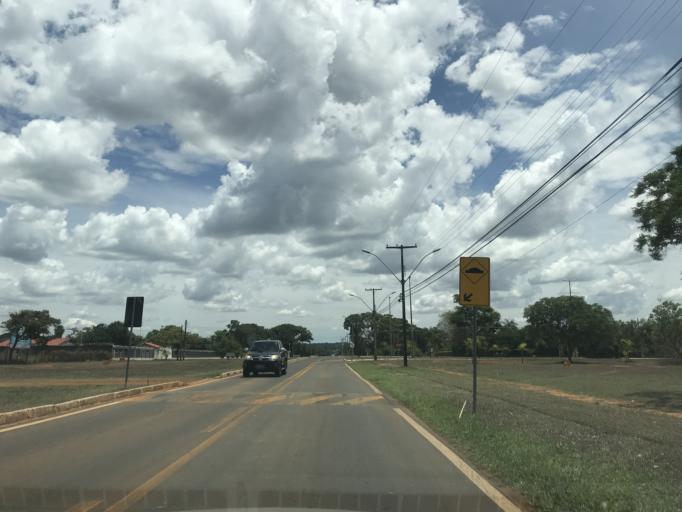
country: BR
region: Federal District
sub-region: Brasilia
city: Brasilia
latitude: -15.9082
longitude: -47.9461
